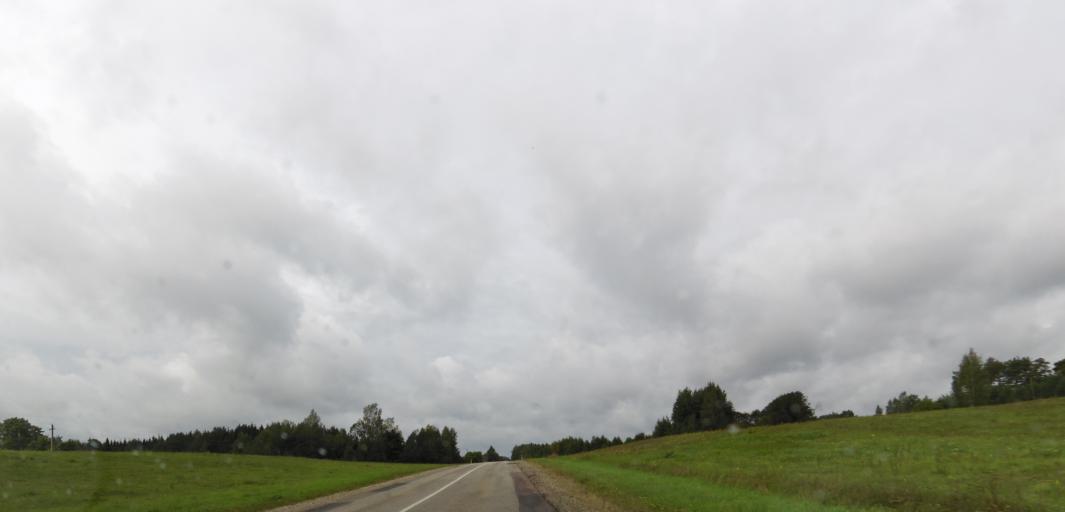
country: LT
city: Moletai
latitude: 55.2121
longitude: 25.3003
